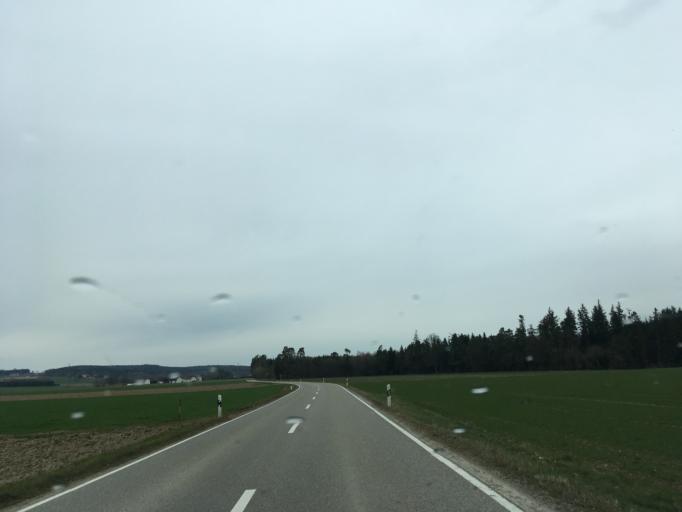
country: DE
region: Bavaria
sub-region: Upper Bavaria
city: Schnaitsee
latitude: 48.0865
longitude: 12.4094
